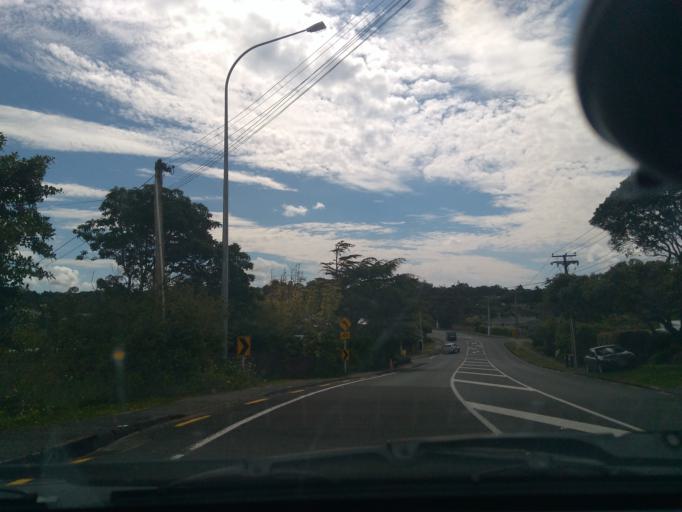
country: NZ
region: Auckland
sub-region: Auckland
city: Waitakere
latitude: -36.9269
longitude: 174.6731
